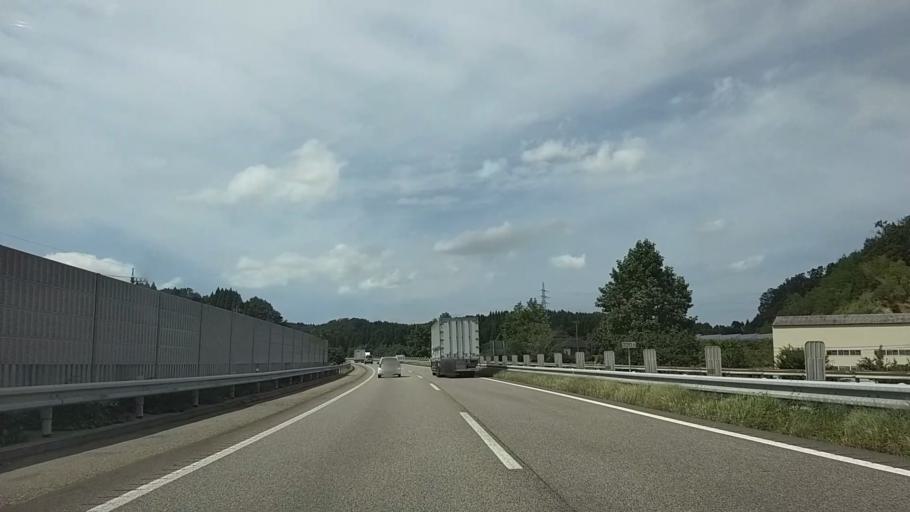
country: JP
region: Toyama
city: Takaoka
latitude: 36.6904
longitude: 137.0711
